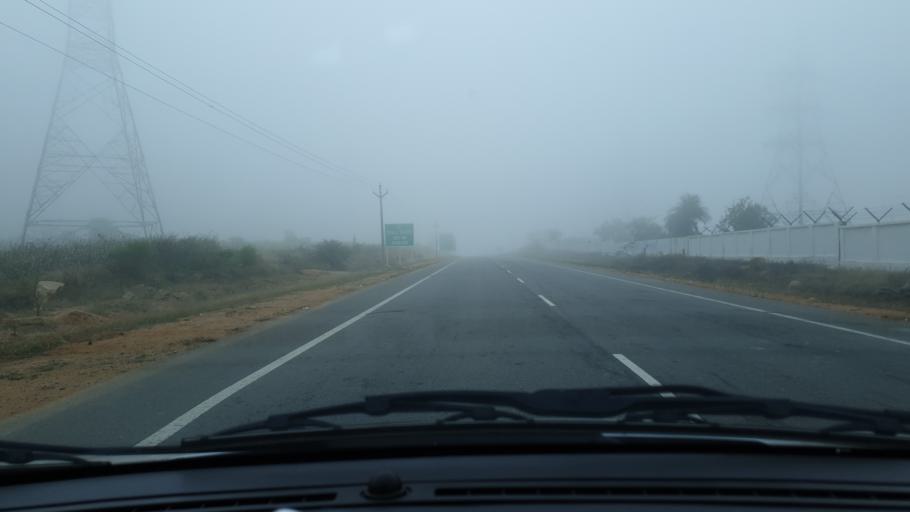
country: IN
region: Telangana
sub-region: Nalgonda
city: Devarkonda
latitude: 16.6169
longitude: 78.6738
